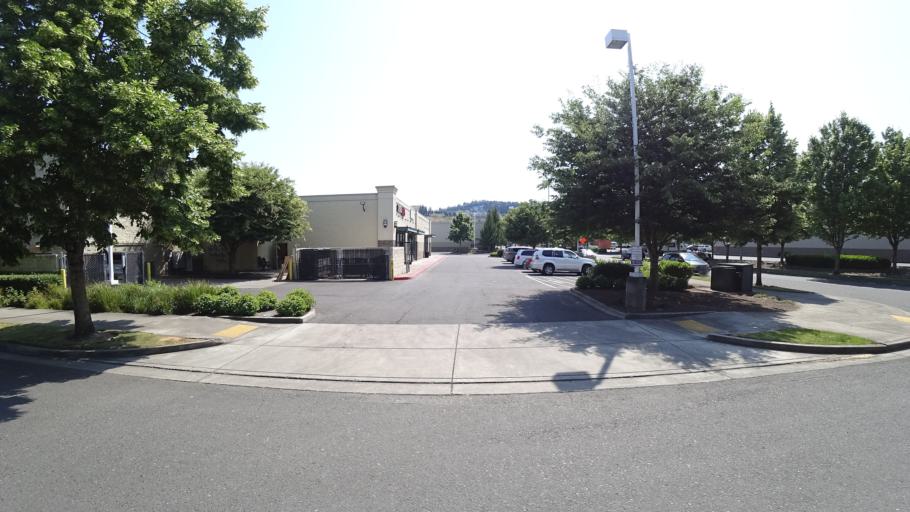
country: US
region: Oregon
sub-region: Multnomah County
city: Lents
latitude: 45.4555
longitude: -122.5813
